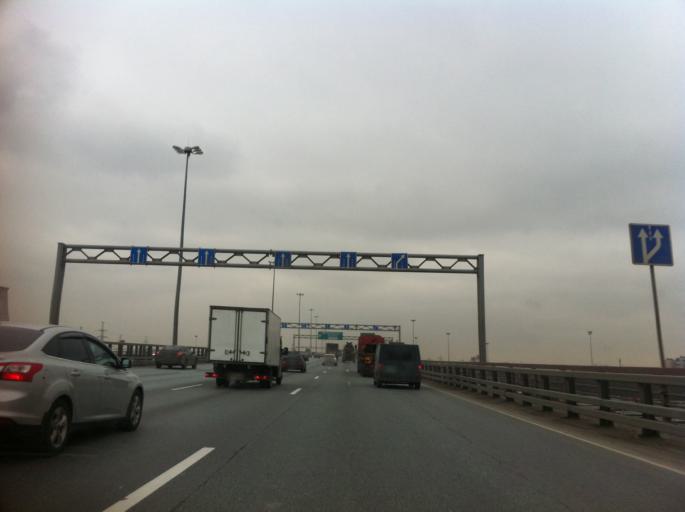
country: RU
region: St.-Petersburg
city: Obukhovo
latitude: 59.8360
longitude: 30.4494
